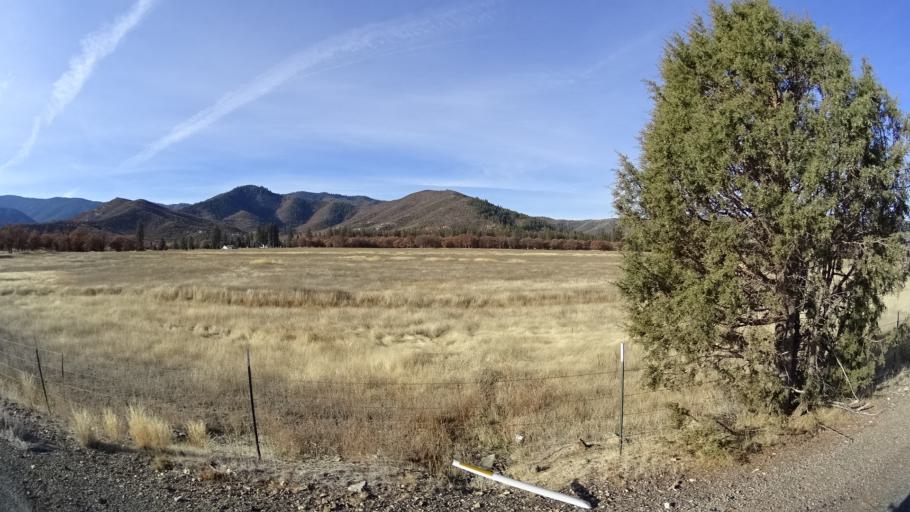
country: US
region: California
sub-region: Siskiyou County
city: Yreka
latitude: 41.6735
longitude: -122.6238
